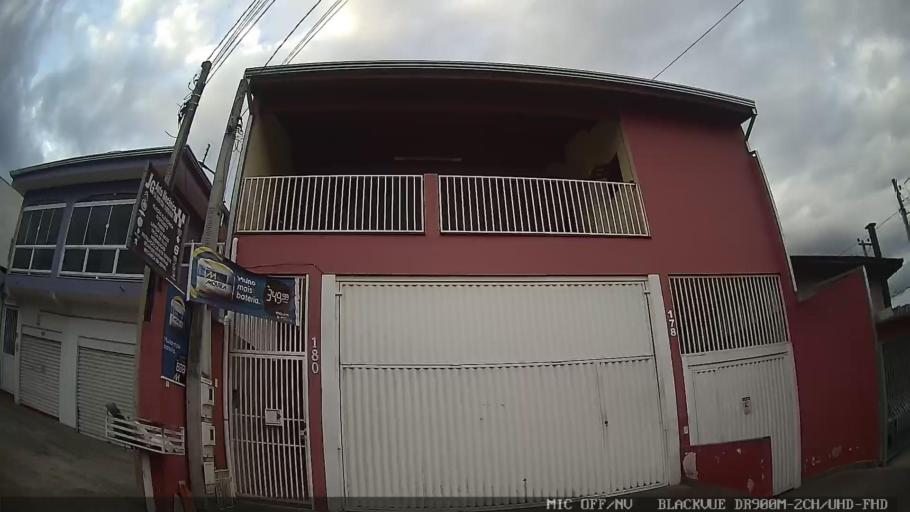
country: BR
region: Sao Paulo
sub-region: Indaiatuba
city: Indaiatuba
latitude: -23.1261
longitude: -47.2355
